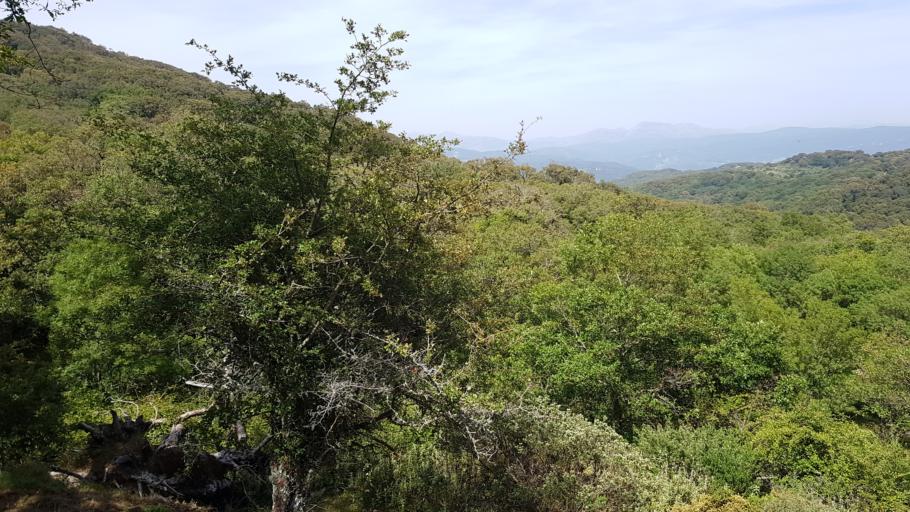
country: ES
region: Andalusia
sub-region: Provincia de Cadiz
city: Alcala de los Gazules
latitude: 36.5157
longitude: -5.5990
